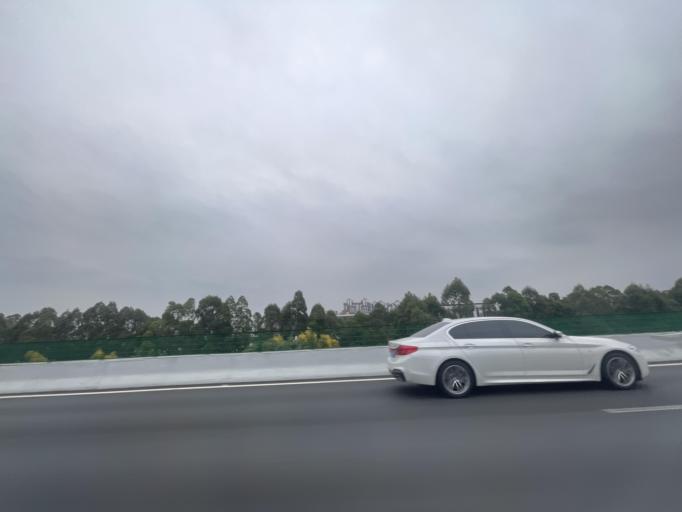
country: CN
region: Guangdong
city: Huangge
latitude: 22.7876
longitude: 113.5225
